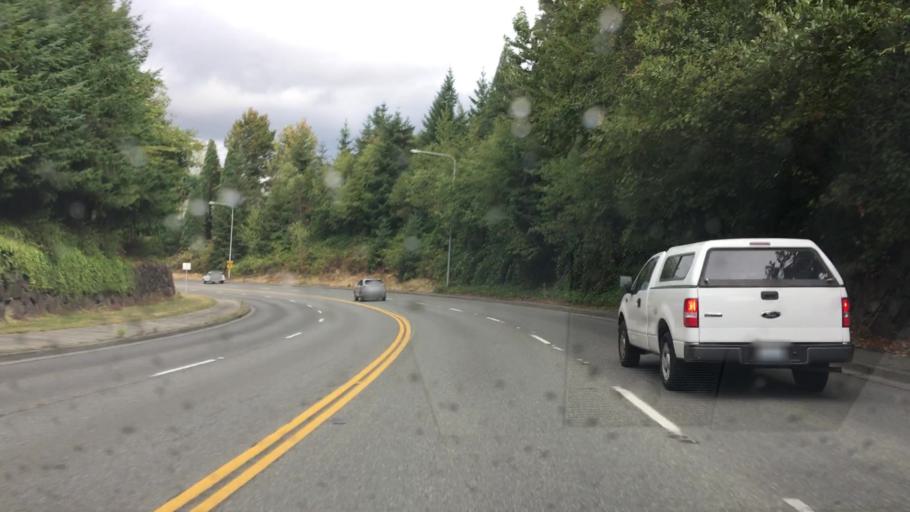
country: US
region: Washington
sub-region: King County
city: Woodinville
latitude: 47.7675
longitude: -122.1508
